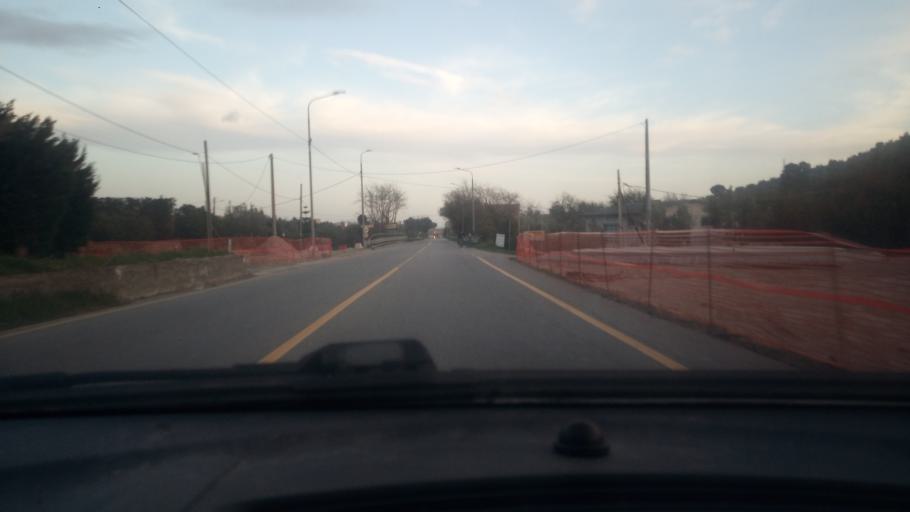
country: IT
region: Calabria
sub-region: Provincia di Catanzaro
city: Barone
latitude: 38.8526
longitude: 16.6368
